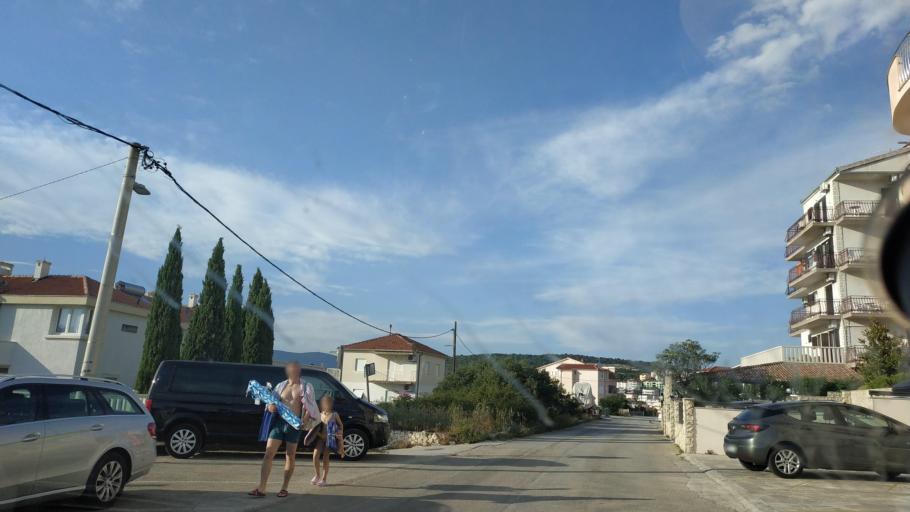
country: HR
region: Splitsko-Dalmatinska
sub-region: Grad Trogir
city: Trogir
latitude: 43.4924
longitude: 16.2575
